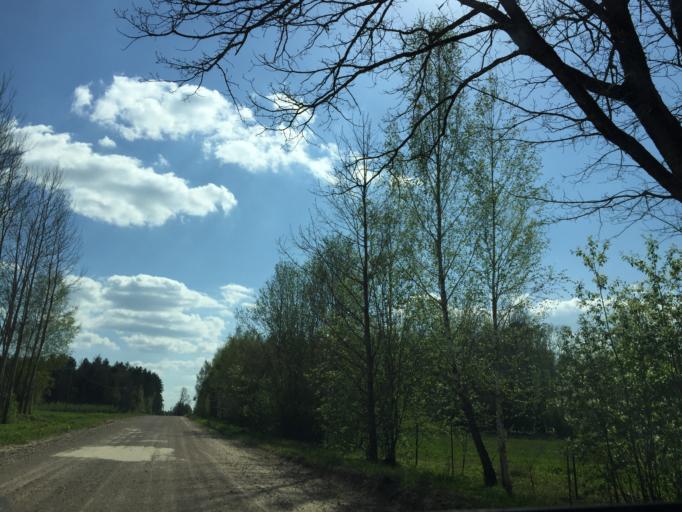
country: LV
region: Vecumnieki
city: Vecumnieki
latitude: 56.4845
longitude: 24.5365
